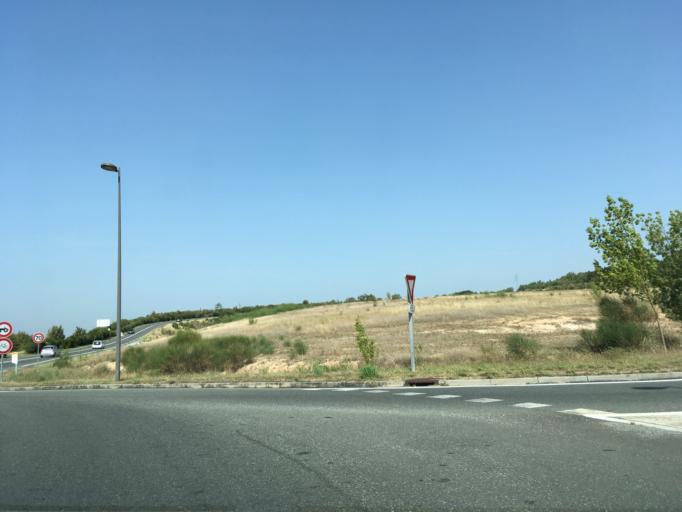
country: FR
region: Midi-Pyrenees
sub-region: Departement du Tarn
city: Lagarrigue
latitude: 43.5689
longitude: 2.2599
